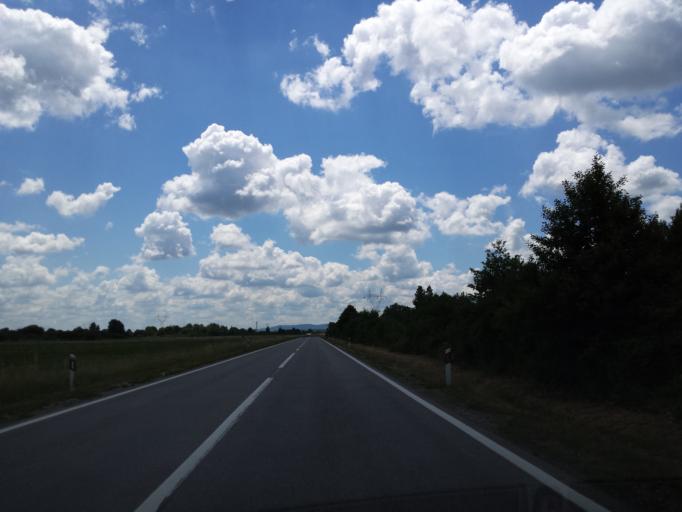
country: HR
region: Sisacko-Moslavacka
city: Lekenik
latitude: 45.5635
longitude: 16.2299
